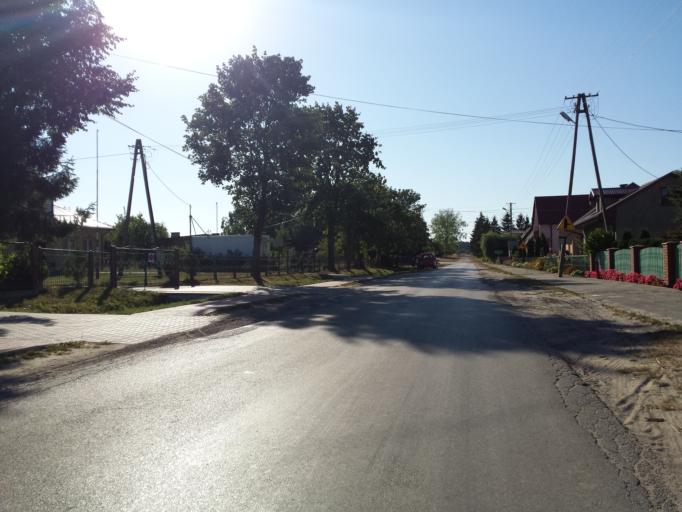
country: PL
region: Swietokrzyskie
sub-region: Powiat buski
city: Gnojno
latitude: 50.6566
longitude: 20.8392
